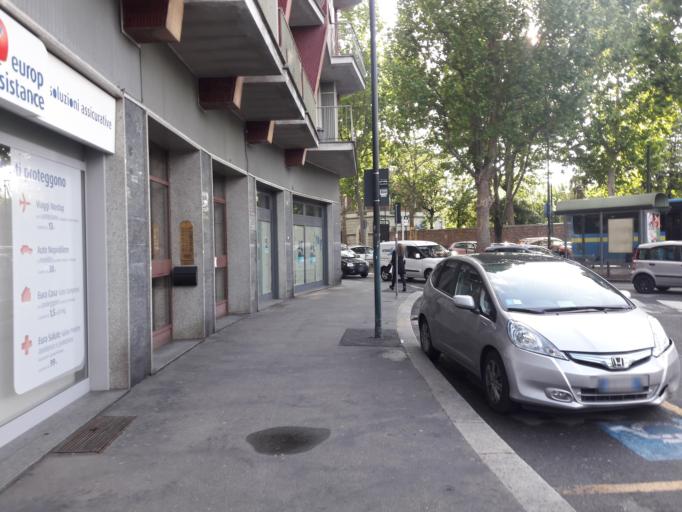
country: IT
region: Piedmont
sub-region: Provincia di Torino
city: Turin
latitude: 45.0464
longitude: 7.6623
